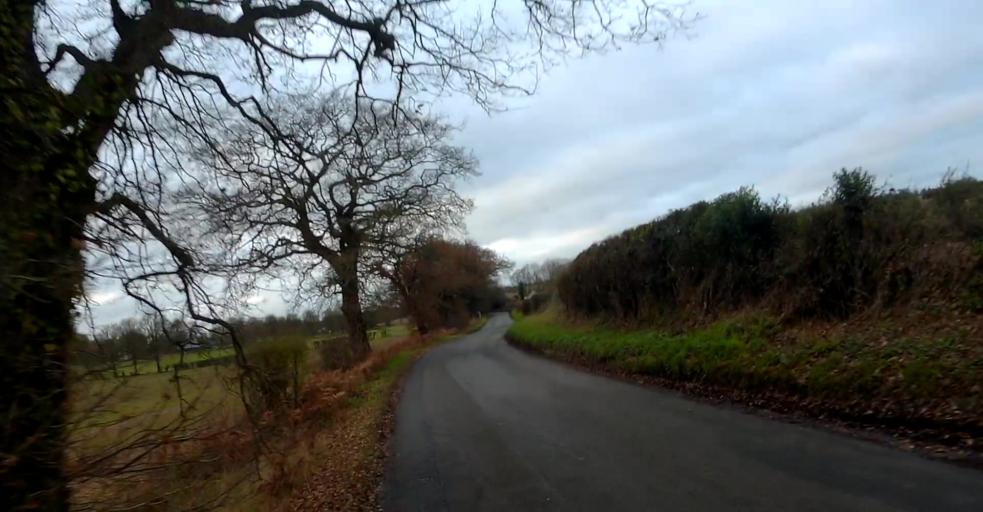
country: GB
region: England
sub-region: Hampshire
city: Overton
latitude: 51.1993
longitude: -1.1705
